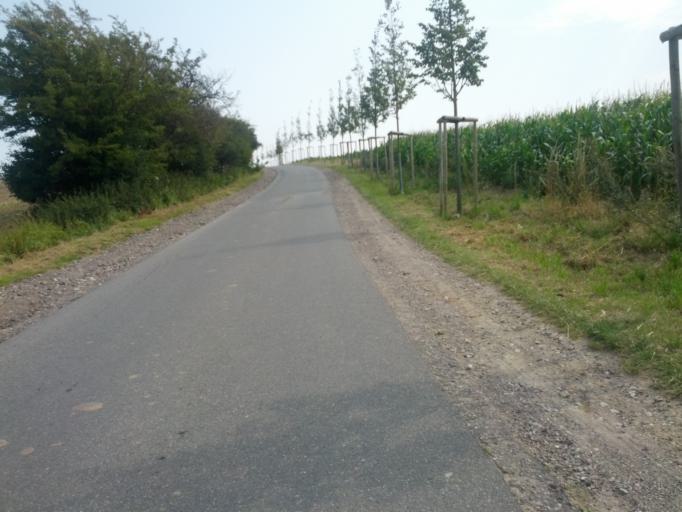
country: DE
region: Mecklenburg-Vorpommern
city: Bastorf
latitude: 54.1310
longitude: 11.6678
